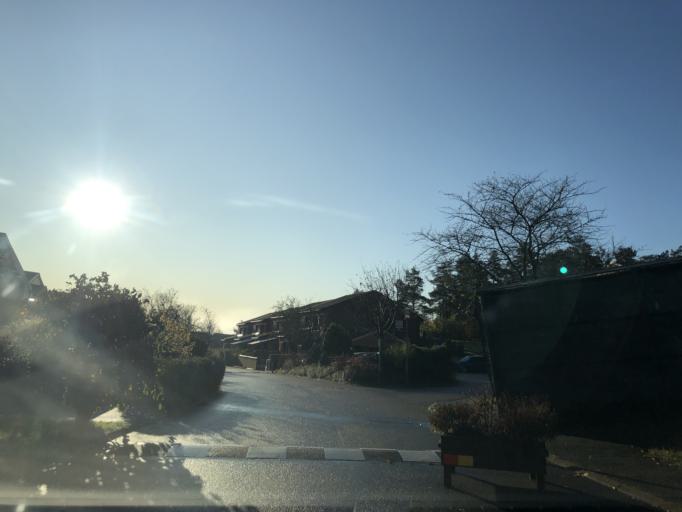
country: SE
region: Vaestra Goetaland
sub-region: Goteborg
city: Rannebergen
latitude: 57.8012
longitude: 12.0613
